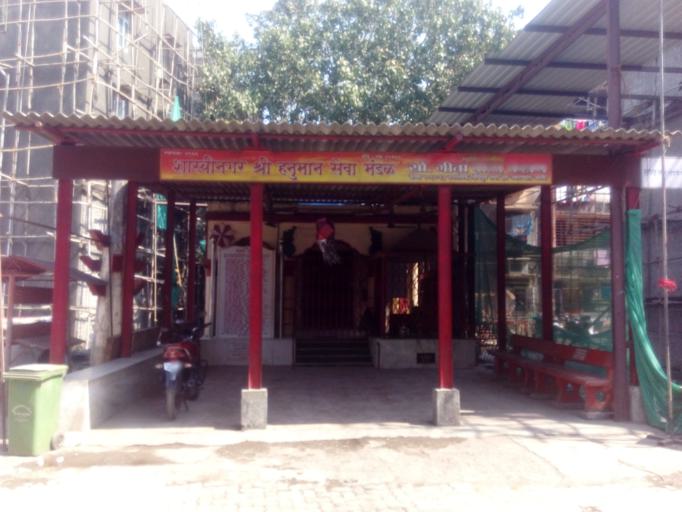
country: IN
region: Maharashtra
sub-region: Mumbai Suburban
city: Mumbai
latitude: 19.0885
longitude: 72.8345
